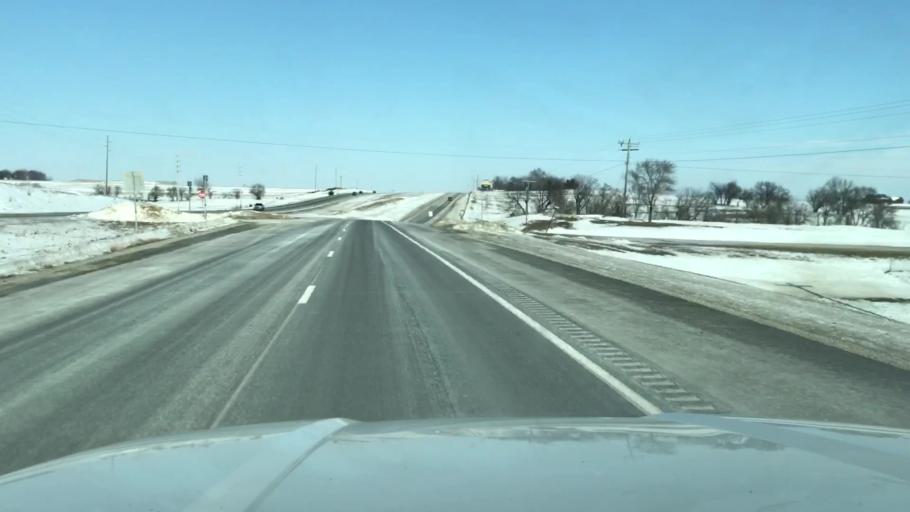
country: US
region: Missouri
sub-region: Andrew County
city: Savannah
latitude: 40.1058
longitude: -94.8696
